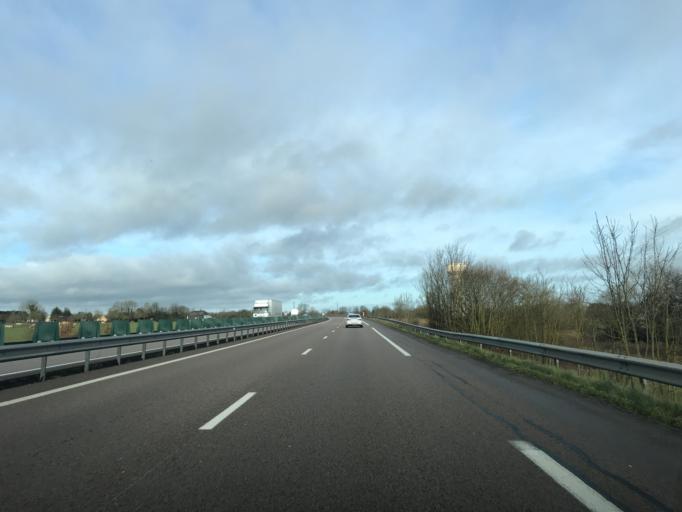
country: FR
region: Haute-Normandie
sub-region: Departement de l'Eure
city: Beuzeville
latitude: 49.3343
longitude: 0.3860
